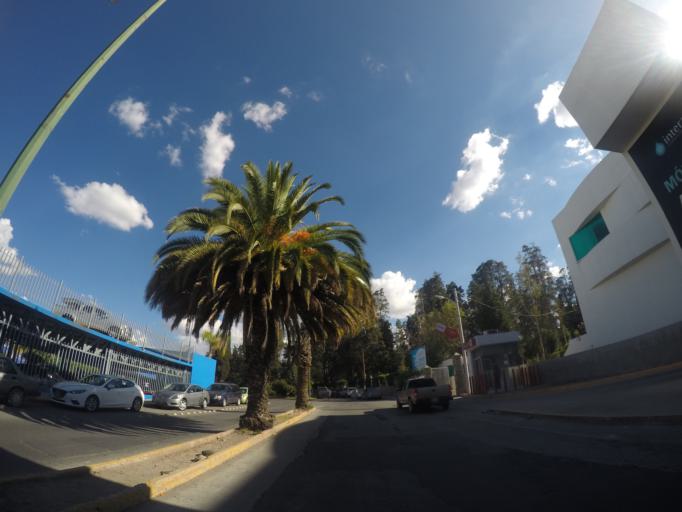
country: MX
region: San Luis Potosi
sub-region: San Luis Potosi
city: San Luis Potosi
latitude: 22.1490
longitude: -101.0197
